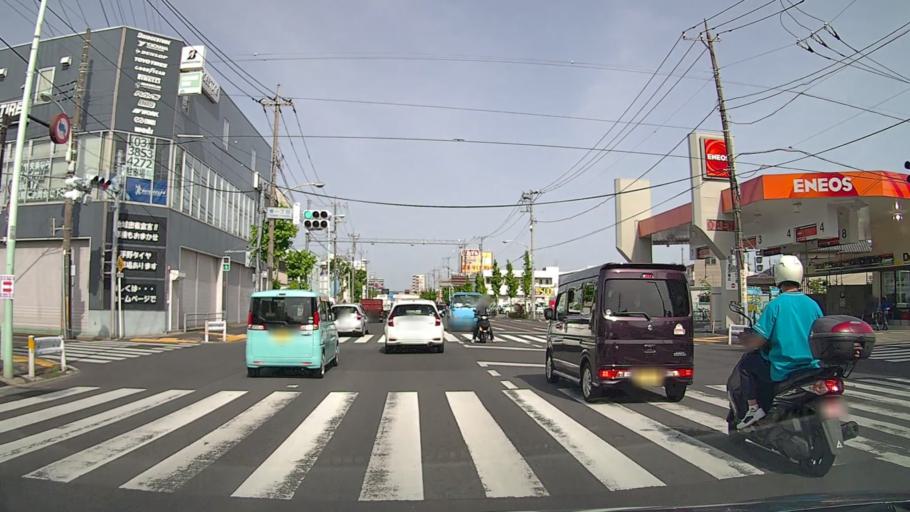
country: JP
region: Saitama
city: Kawaguchi
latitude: 35.7783
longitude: 139.7605
